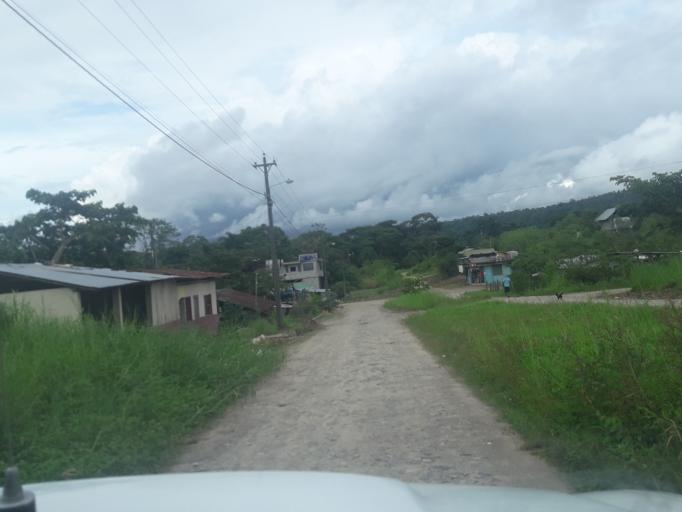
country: EC
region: Napo
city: Archidona
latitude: -0.9467
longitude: -77.8159
